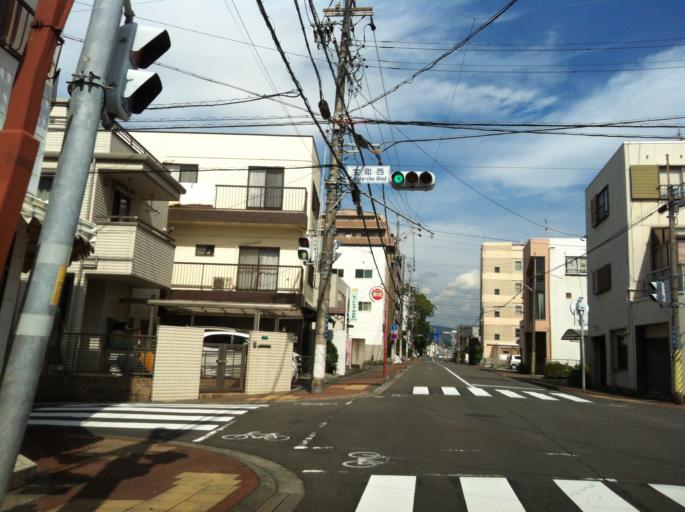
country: JP
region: Shizuoka
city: Shizuoka-shi
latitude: 35.0208
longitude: 138.4819
